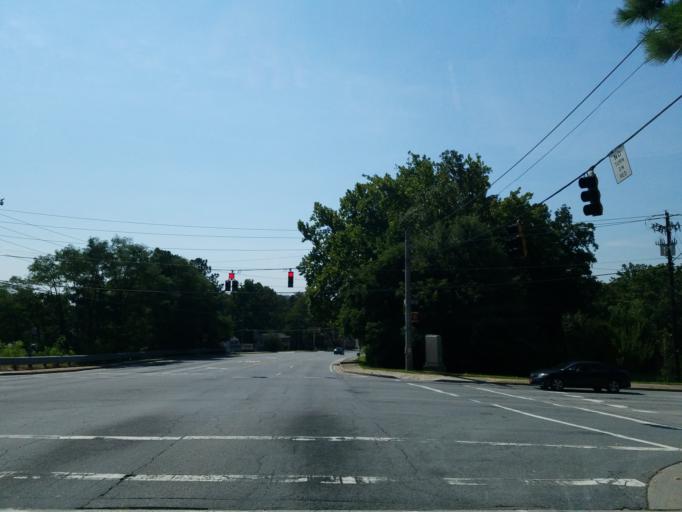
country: US
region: Georgia
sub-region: DeKalb County
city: Chamblee
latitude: 33.8854
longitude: -84.3103
